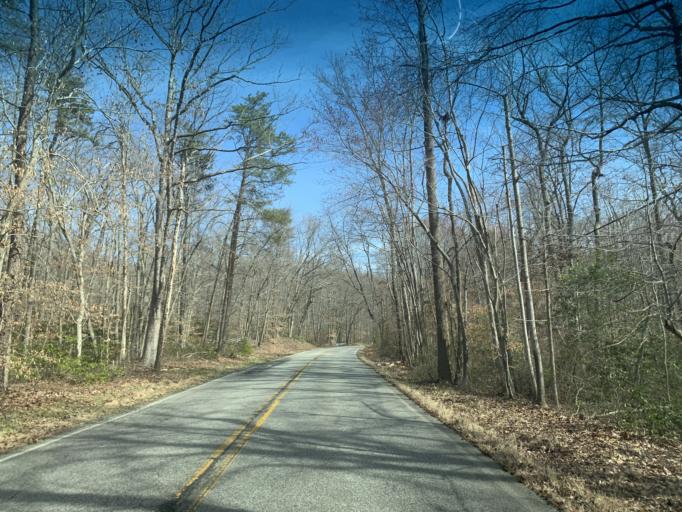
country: US
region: Maryland
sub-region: Cecil County
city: Charlestown
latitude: 39.5643
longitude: -76.0042
